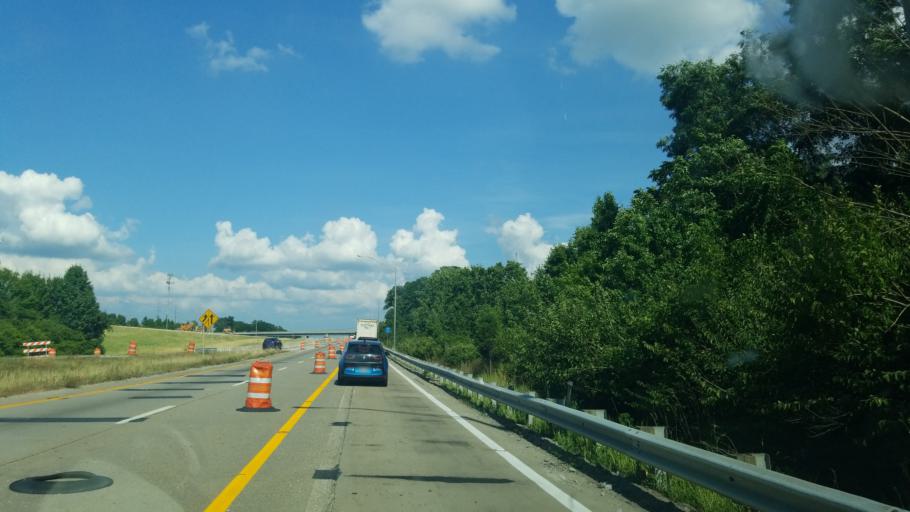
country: US
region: Kentucky
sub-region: Kenton County
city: Crestview Hills
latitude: 39.0326
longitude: -84.5983
